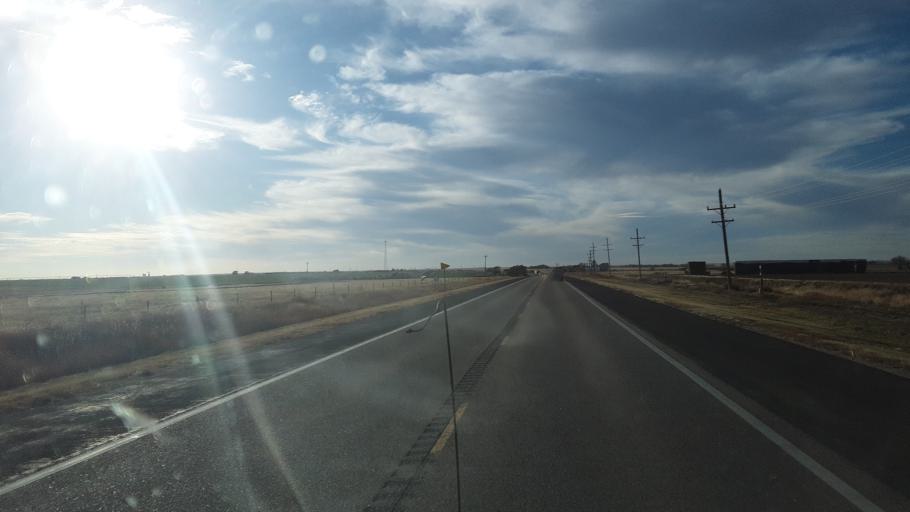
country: US
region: Kansas
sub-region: Kearny County
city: Lakin
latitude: 37.9736
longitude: -101.1777
